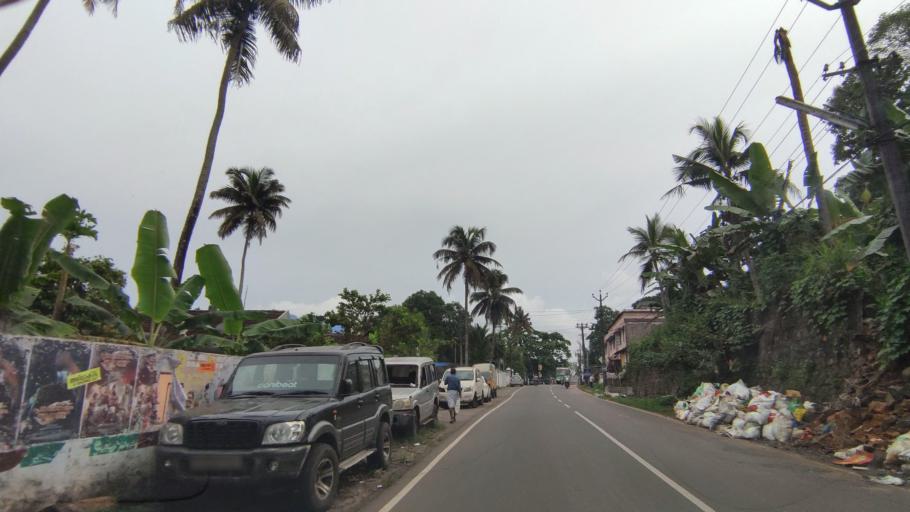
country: IN
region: Kerala
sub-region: Kottayam
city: Kottayam
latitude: 9.5870
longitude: 76.5172
